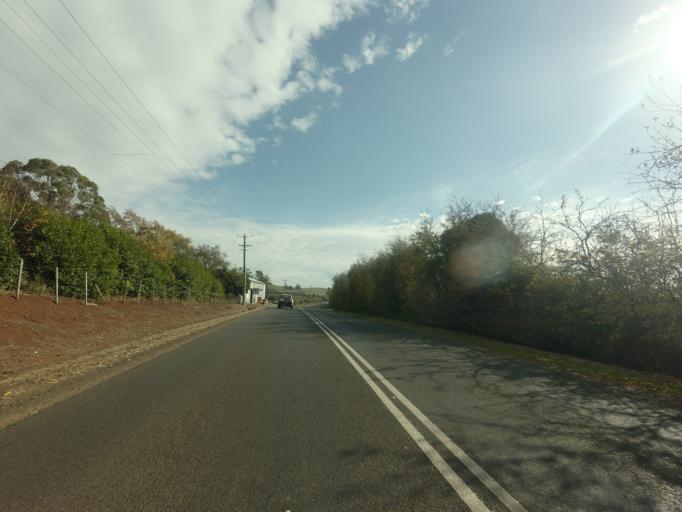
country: AU
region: Tasmania
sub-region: Meander Valley
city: Deloraine
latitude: -41.5231
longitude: 146.7439
